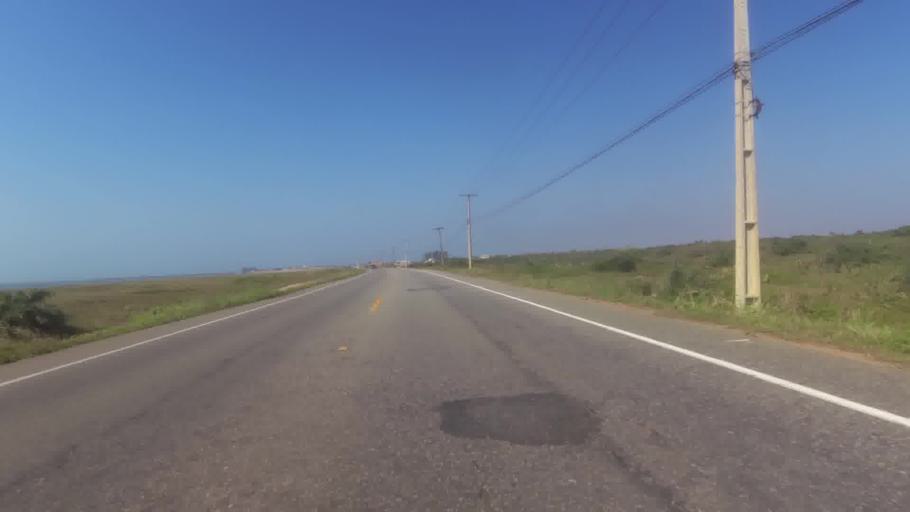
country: BR
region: Espirito Santo
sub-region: Itapemirim
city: Itapemirim
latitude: -20.9817
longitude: -40.8119
